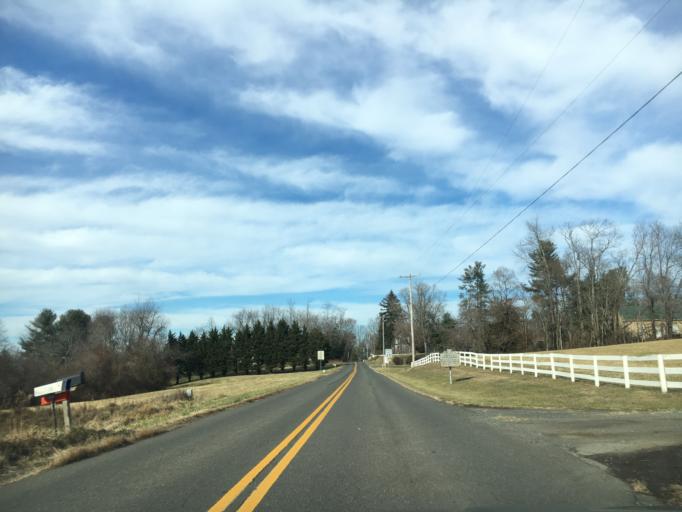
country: US
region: Virginia
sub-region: Fauquier County
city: Marshall
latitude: 38.7473
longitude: -77.9614
